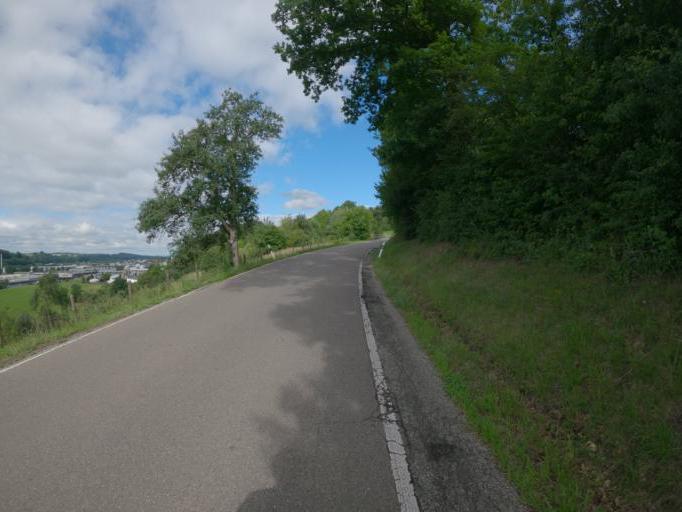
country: DE
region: Baden-Wuerttemberg
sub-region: Regierungsbezirk Stuttgart
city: Ebersbach an der Fils
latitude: 48.7223
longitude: 9.5552
